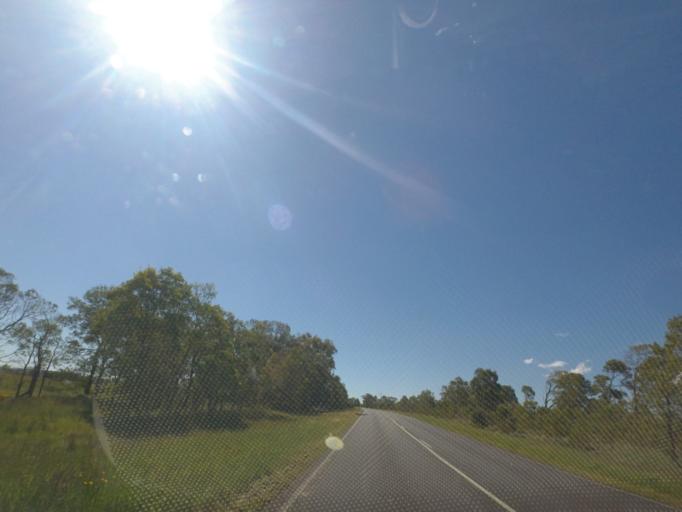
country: AU
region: Victoria
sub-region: Moorabool
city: Bacchus Marsh
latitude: -37.6304
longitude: 144.2149
